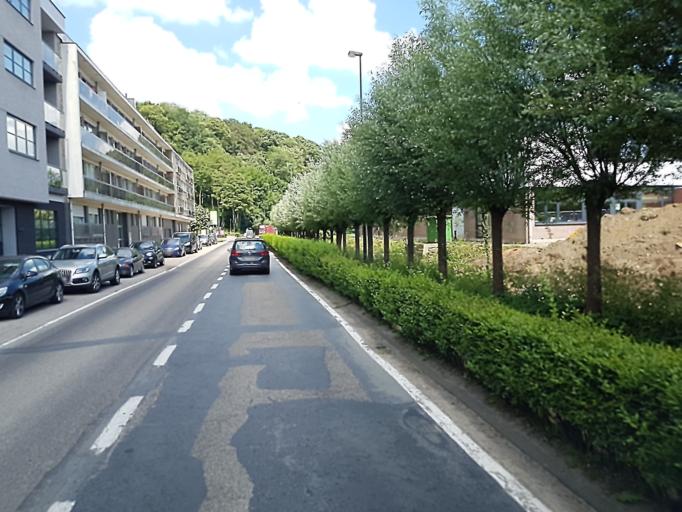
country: BE
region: Flanders
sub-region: Provincie Vlaams-Brabant
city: Hoeilaart
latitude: 50.7688
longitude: 4.4783
